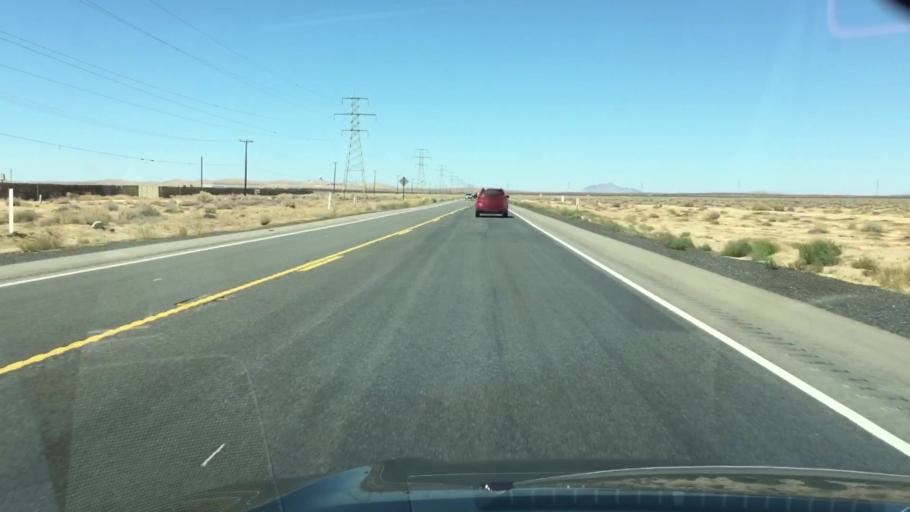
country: US
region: California
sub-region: Kern County
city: Boron
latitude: 35.0136
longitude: -117.5475
